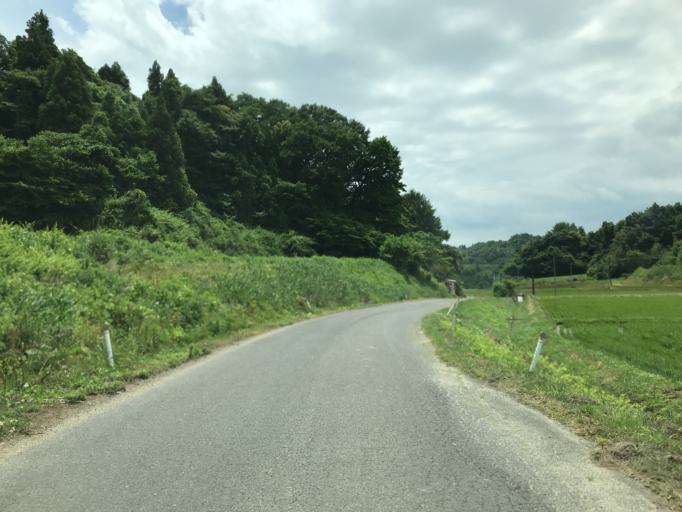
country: JP
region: Fukushima
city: Miharu
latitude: 37.4022
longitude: 140.5234
